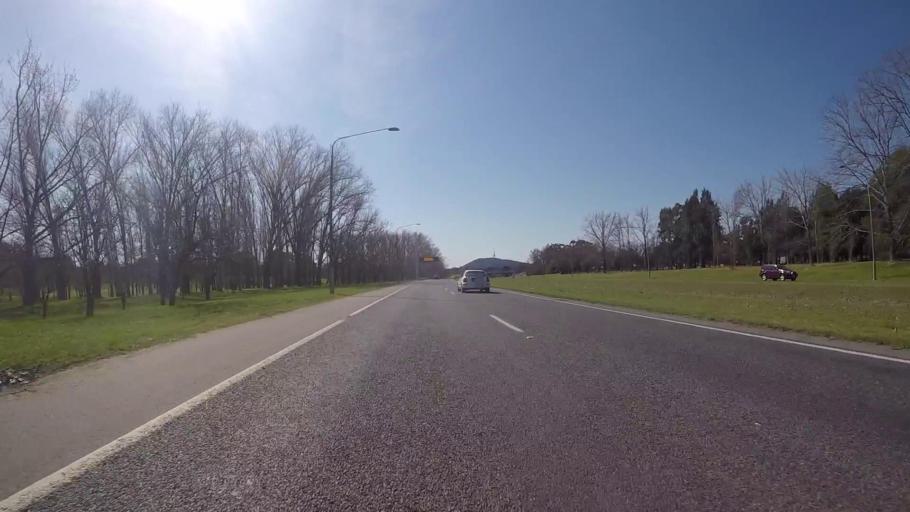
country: AU
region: Australian Capital Territory
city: Forrest
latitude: -35.3318
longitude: 149.0860
